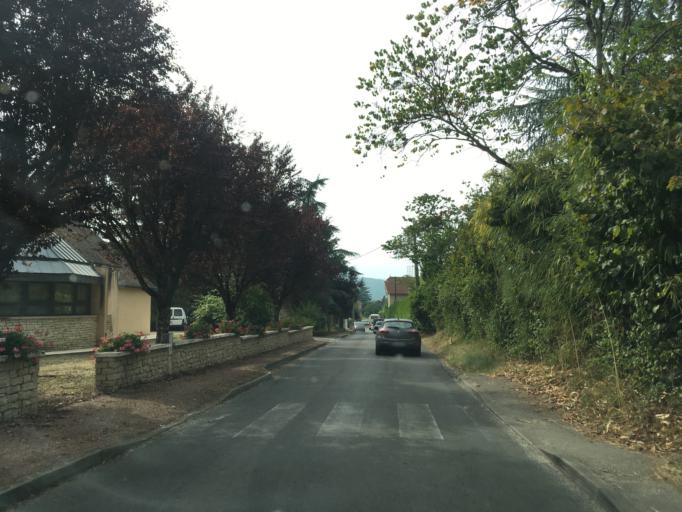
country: FR
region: Midi-Pyrenees
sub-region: Departement du Lot
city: Souillac
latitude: 44.8551
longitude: 1.5129
